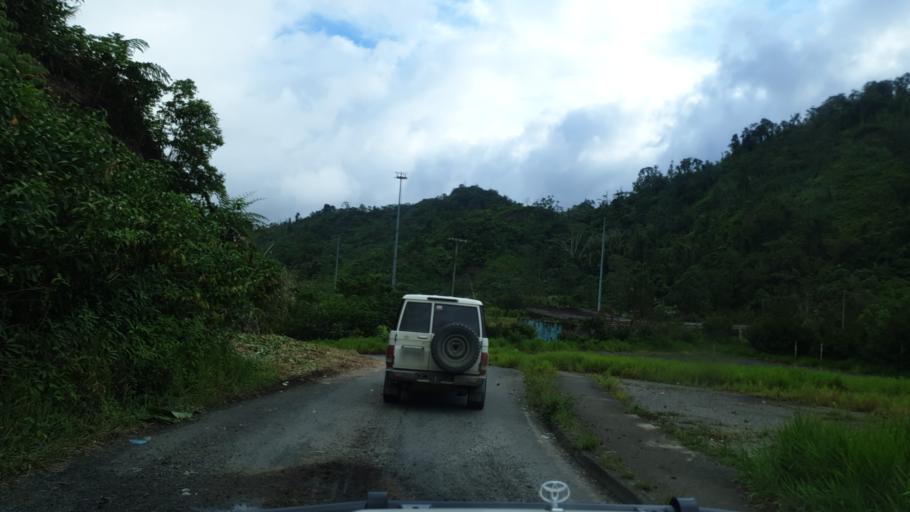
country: PG
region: Bougainville
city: Panguna
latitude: -6.3053
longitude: 155.4880
